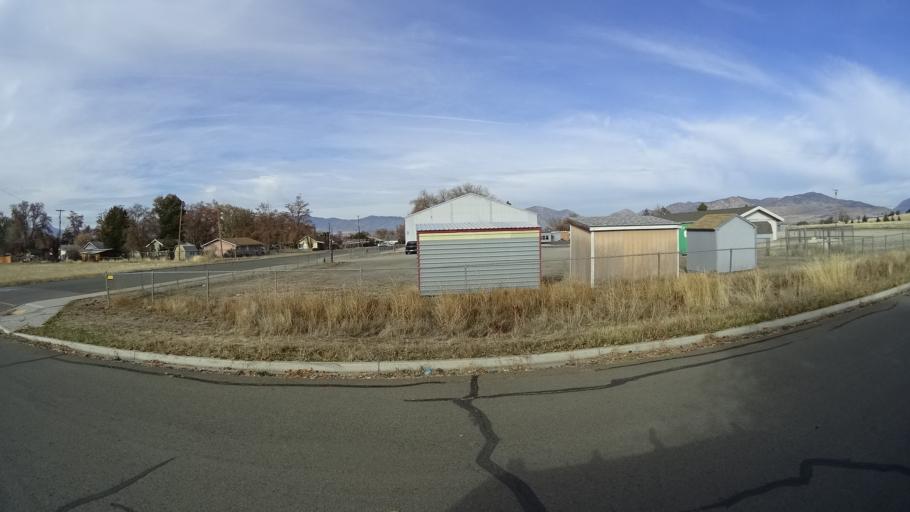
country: US
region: California
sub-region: Siskiyou County
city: Montague
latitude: 41.7268
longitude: -122.5197
